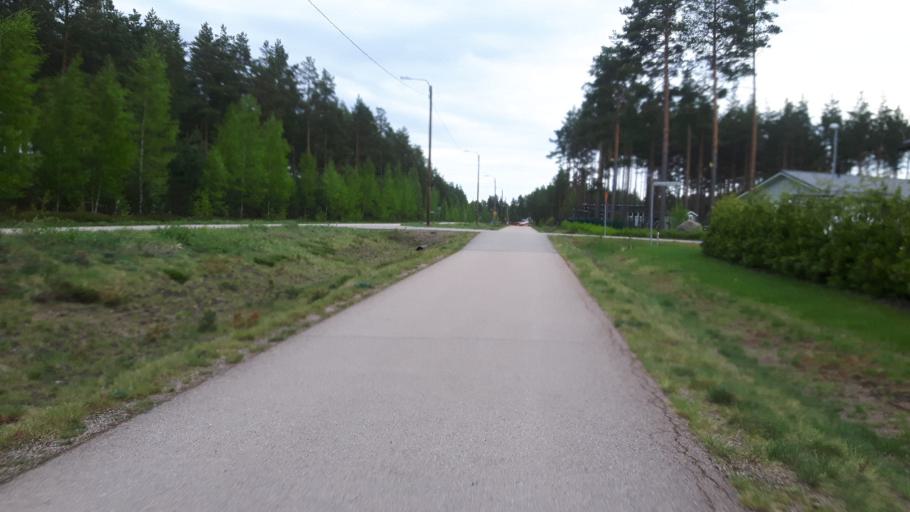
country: FI
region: Kymenlaakso
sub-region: Kotka-Hamina
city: Hamina
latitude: 60.5419
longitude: 27.2301
